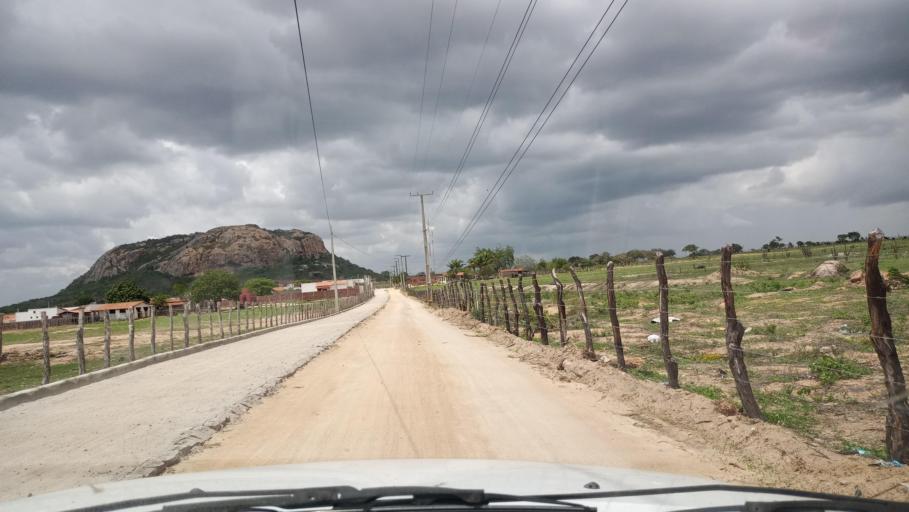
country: BR
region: Rio Grande do Norte
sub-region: Tangara
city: Tangara
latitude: -6.0982
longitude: -35.7124
